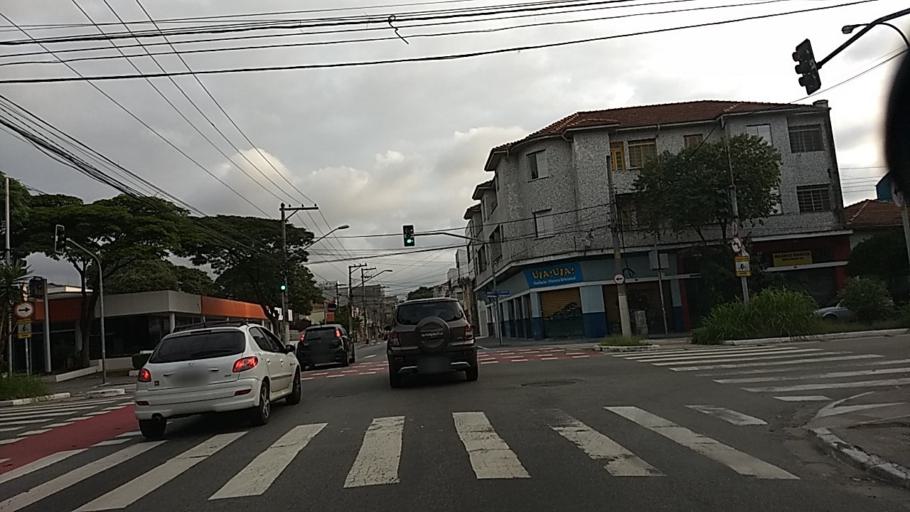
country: BR
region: Sao Paulo
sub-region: Sao Paulo
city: Sao Paulo
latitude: -23.5284
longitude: -46.6089
